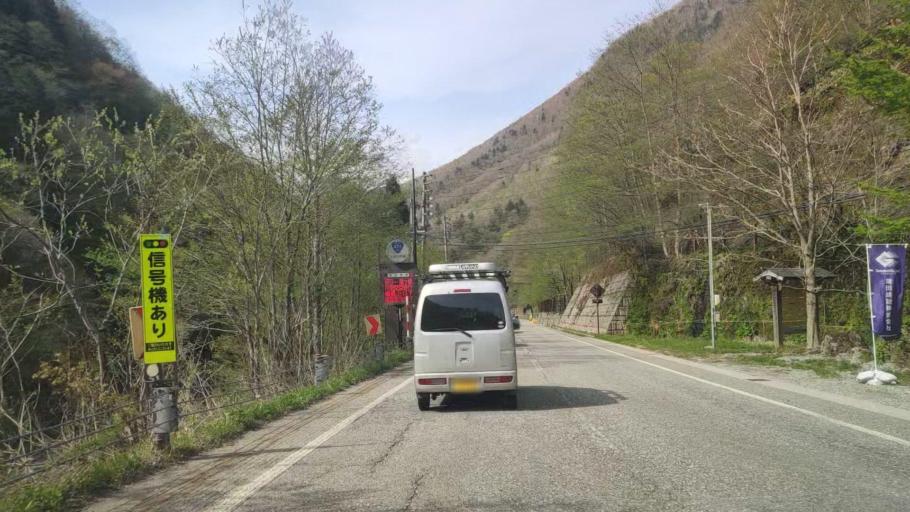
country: JP
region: Gifu
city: Takayama
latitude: 36.1997
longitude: 137.5512
